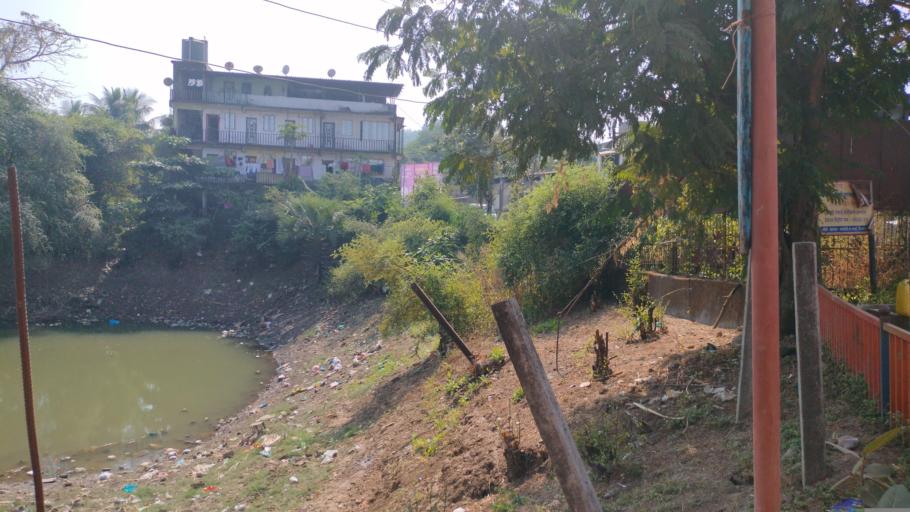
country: IN
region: Maharashtra
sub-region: Thane
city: Bhayandar
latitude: 19.3643
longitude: 72.8816
